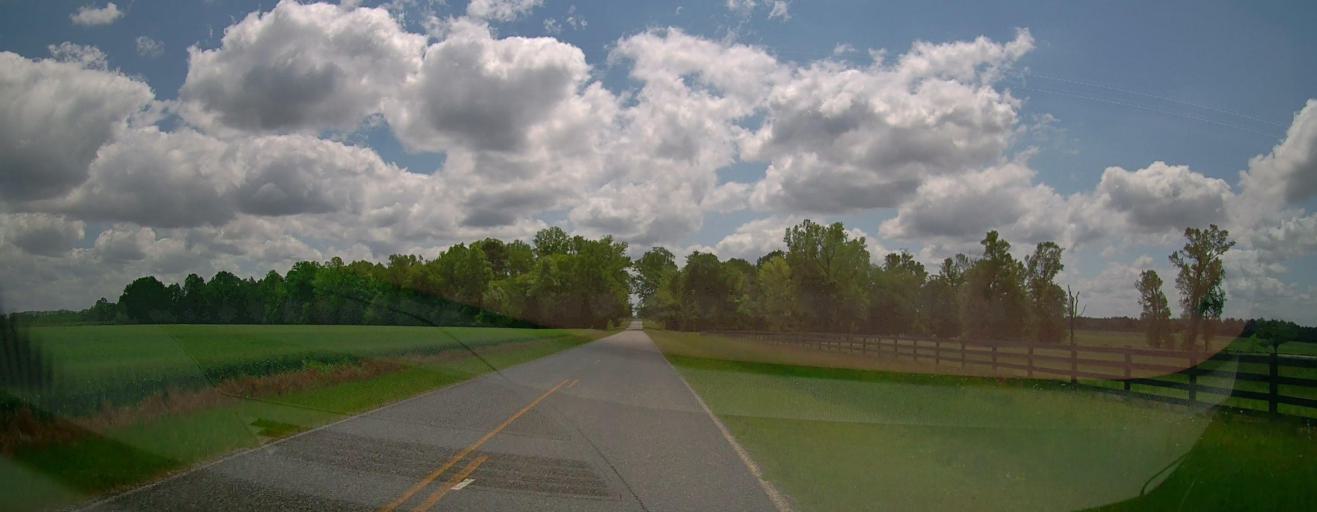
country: US
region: Georgia
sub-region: Dodge County
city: Chester
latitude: 32.5464
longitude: -83.1401
